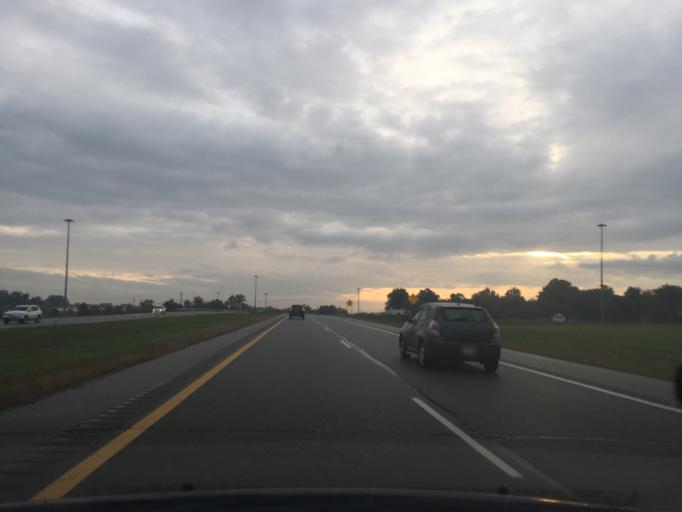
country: US
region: Michigan
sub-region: Oakland County
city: Pontiac
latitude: 42.6438
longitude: -83.2728
